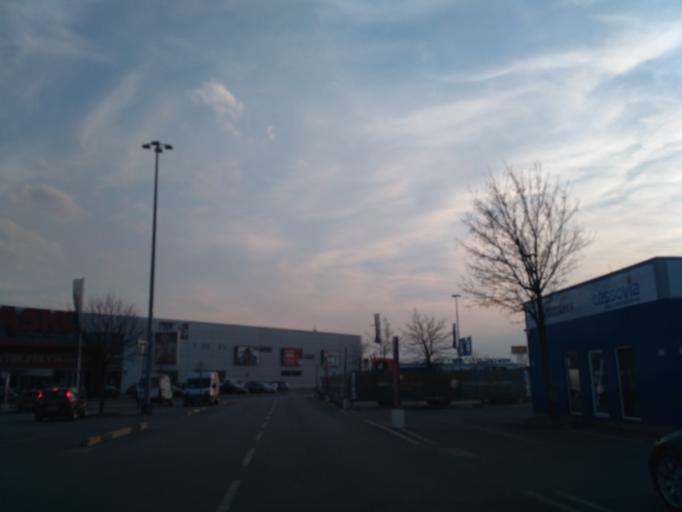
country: SK
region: Kosicky
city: Kosice
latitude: 48.6968
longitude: 21.2495
